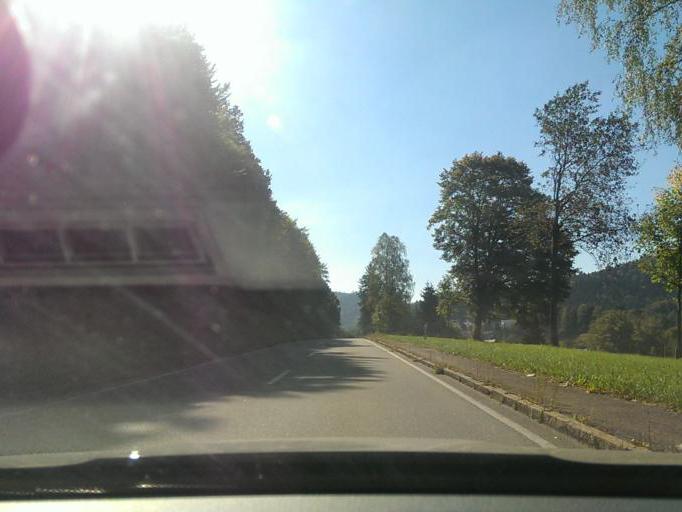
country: DE
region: Baden-Wuerttemberg
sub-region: Karlsruhe Region
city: Bad Herrenalb
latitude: 48.8164
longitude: 8.4455
